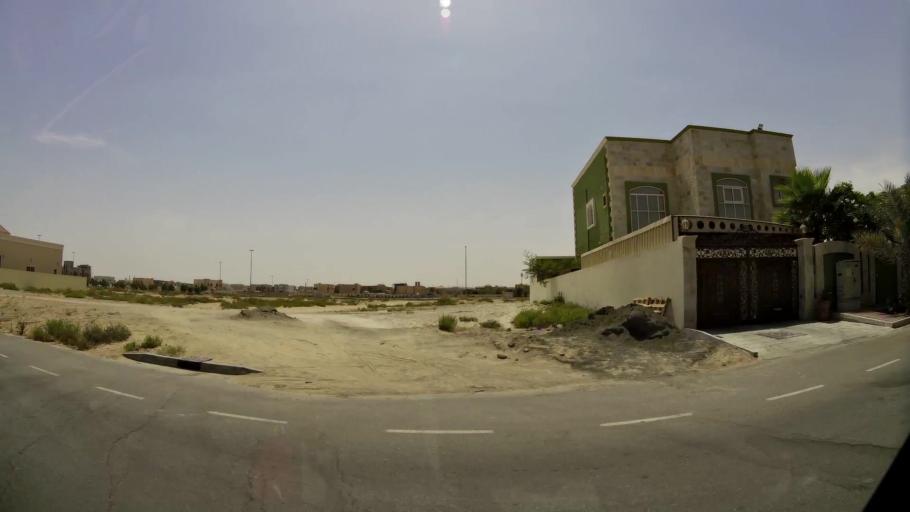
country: AE
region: Ash Shariqah
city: Sharjah
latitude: 25.1834
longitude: 55.4263
